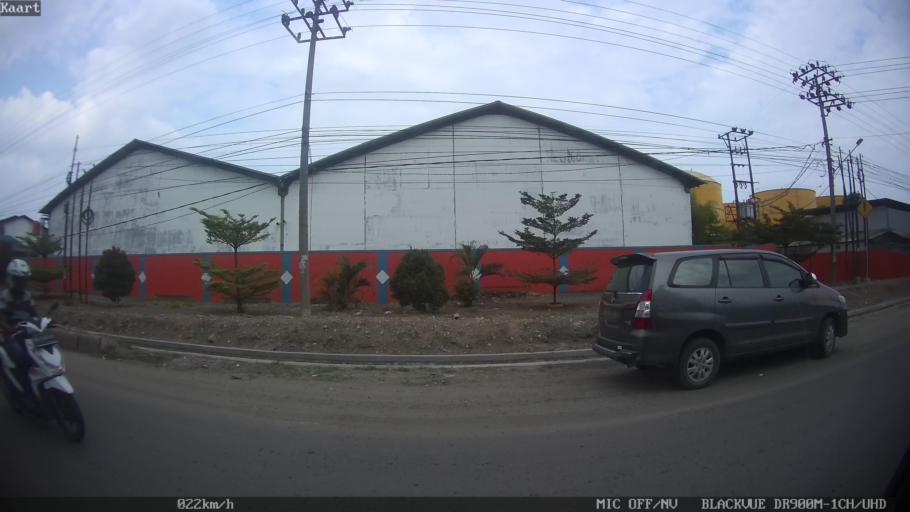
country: ID
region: Lampung
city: Panjang
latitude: -5.4585
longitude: 105.3138
